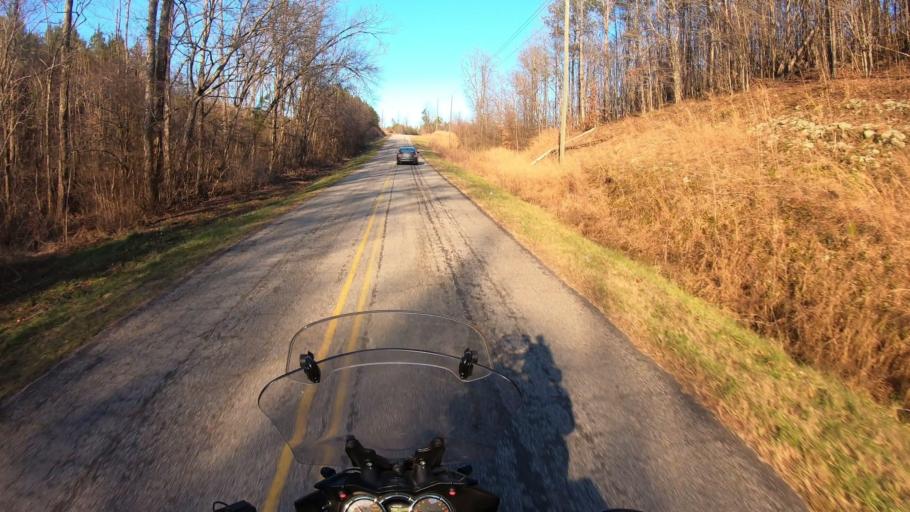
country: US
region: Georgia
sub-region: Haralson County
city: Tallapoosa
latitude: 33.7898
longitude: -85.4478
